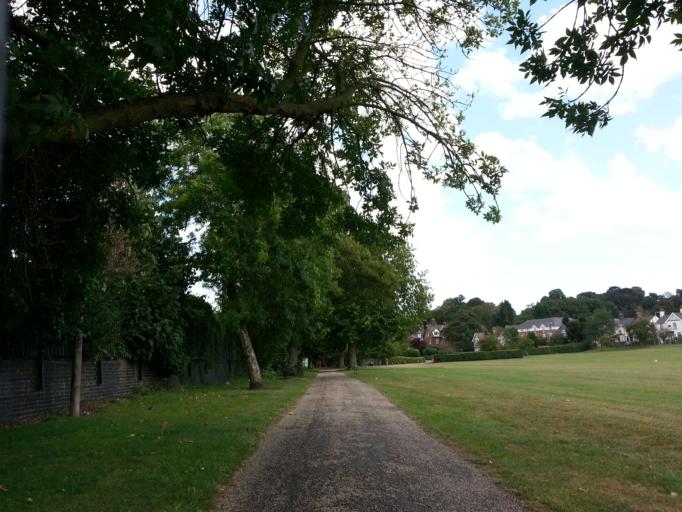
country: GB
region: England
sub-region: Suffolk
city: Ipswich
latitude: 52.0514
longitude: 1.1388
